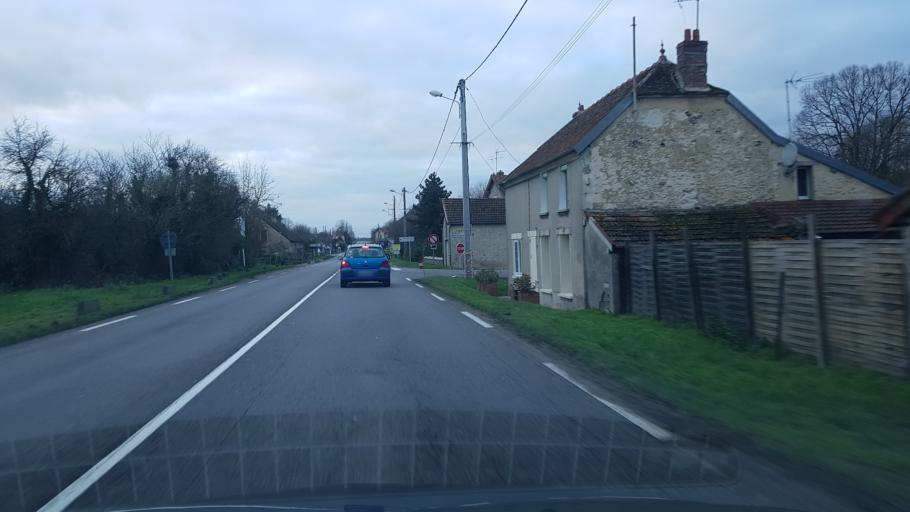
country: FR
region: Champagne-Ardenne
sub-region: Departement de la Marne
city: Esternay
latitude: 48.7140
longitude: 3.4900
